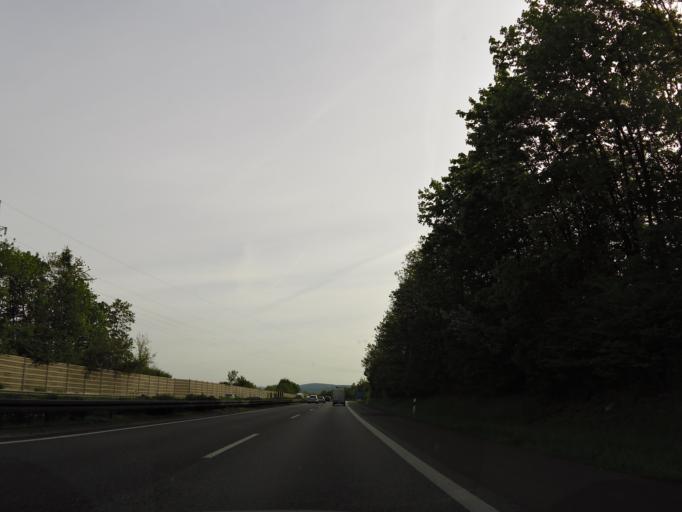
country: DE
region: Lower Saxony
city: Hillerse
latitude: 51.6890
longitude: 9.9303
